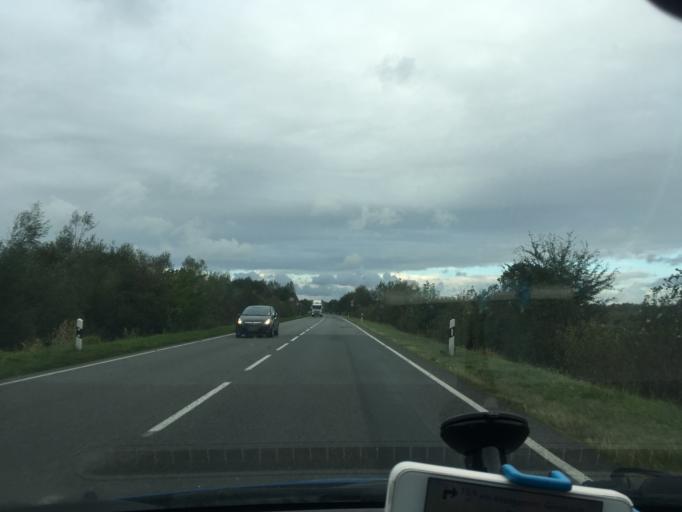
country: DE
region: Lower Saxony
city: Vogelsen
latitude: 53.3149
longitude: 10.3382
